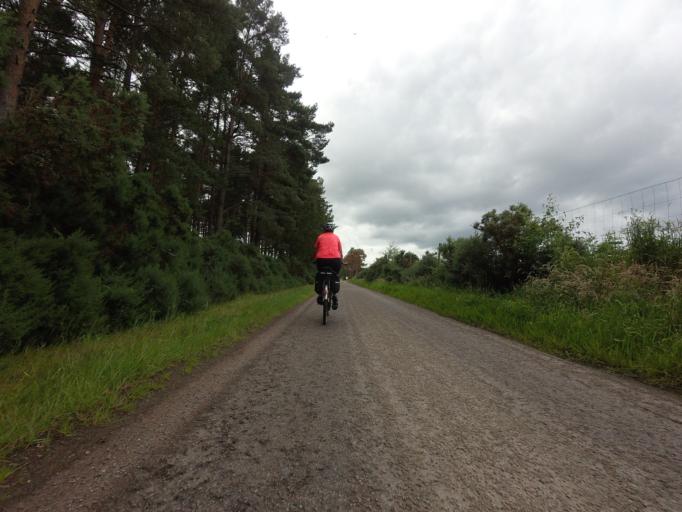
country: GB
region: Scotland
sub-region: Highland
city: Nairn
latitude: 57.6028
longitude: -3.7712
